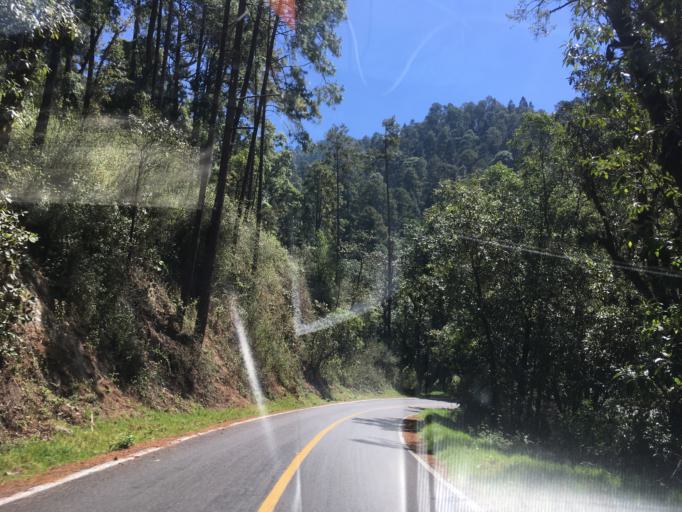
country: MX
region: Michoacan
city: Tzitzio
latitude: 19.6689
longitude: -100.8041
